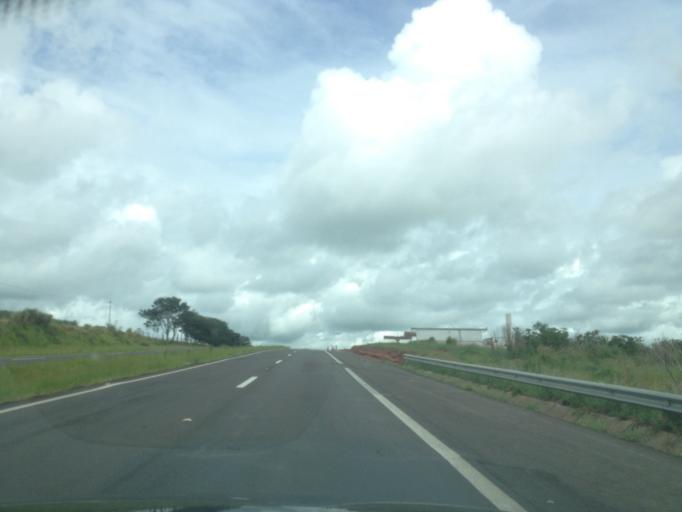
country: BR
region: Sao Paulo
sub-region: Garca
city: Garca
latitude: -22.2638
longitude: -49.5205
